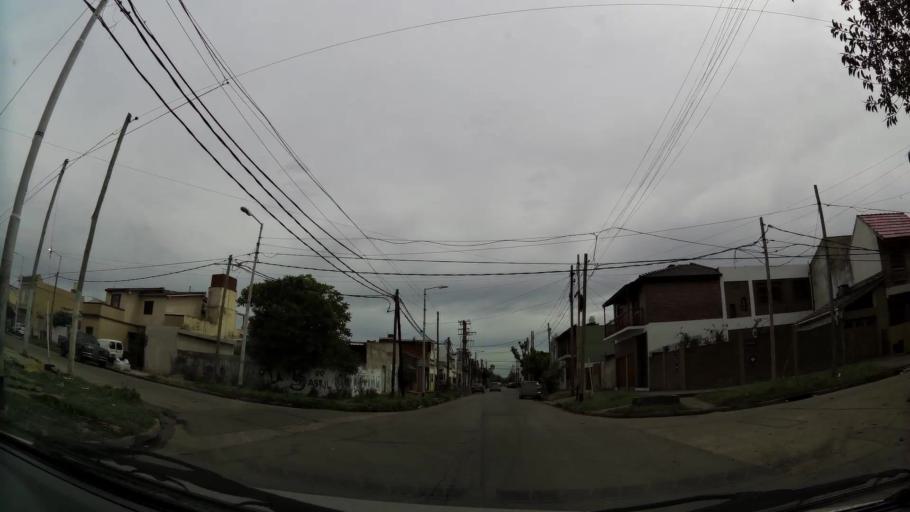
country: AR
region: Buenos Aires
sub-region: Partido de Avellaneda
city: Avellaneda
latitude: -34.6646
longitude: -58.3483
